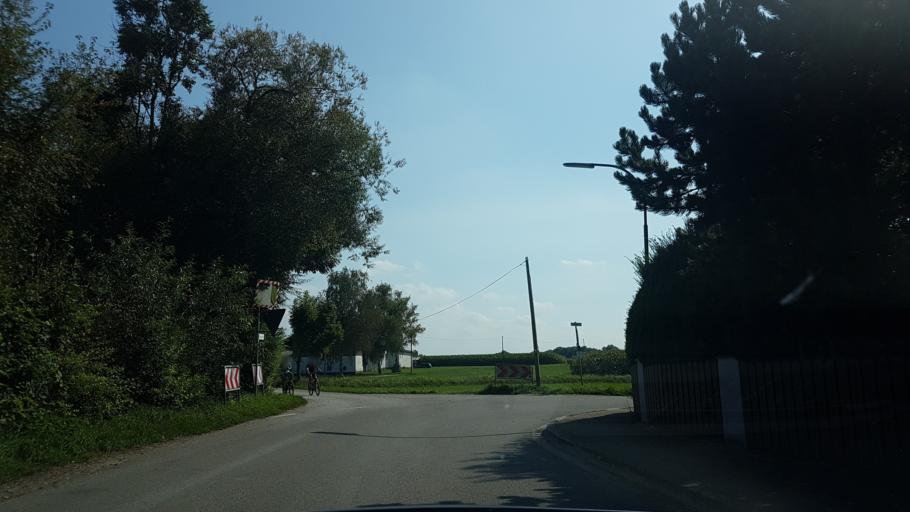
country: DE
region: Bavaria
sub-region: Upper Bavaria
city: Moosinning
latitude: 48.2739
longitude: 11.8281
